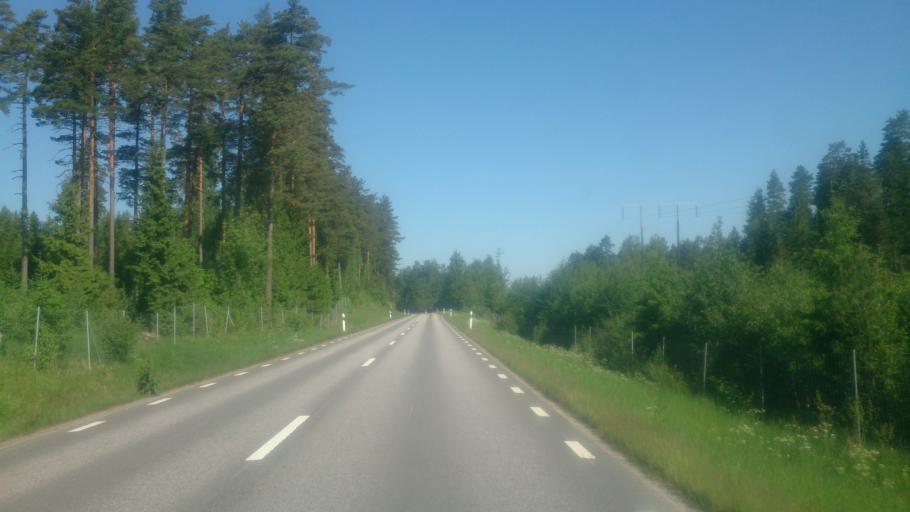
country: SE
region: OEstergoetland
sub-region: Atvidabergs Kommun
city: Atvidaberg
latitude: 58.1603
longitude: 16.0651
